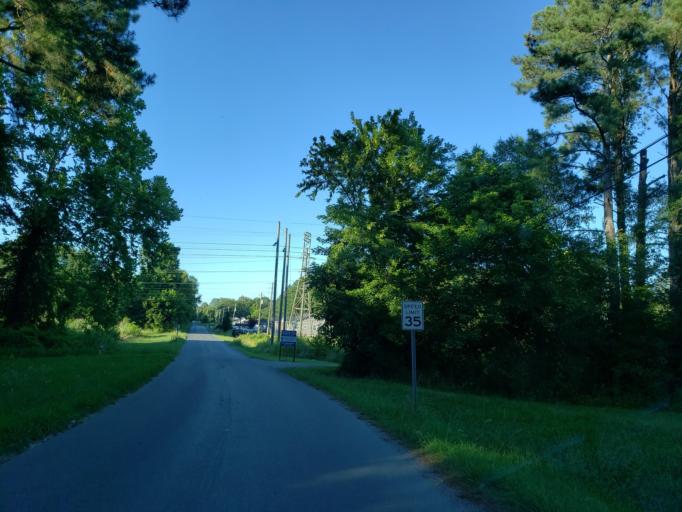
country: US
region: Georgia
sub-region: Polk County
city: Aragon
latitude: 34.0478
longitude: -85.0541
